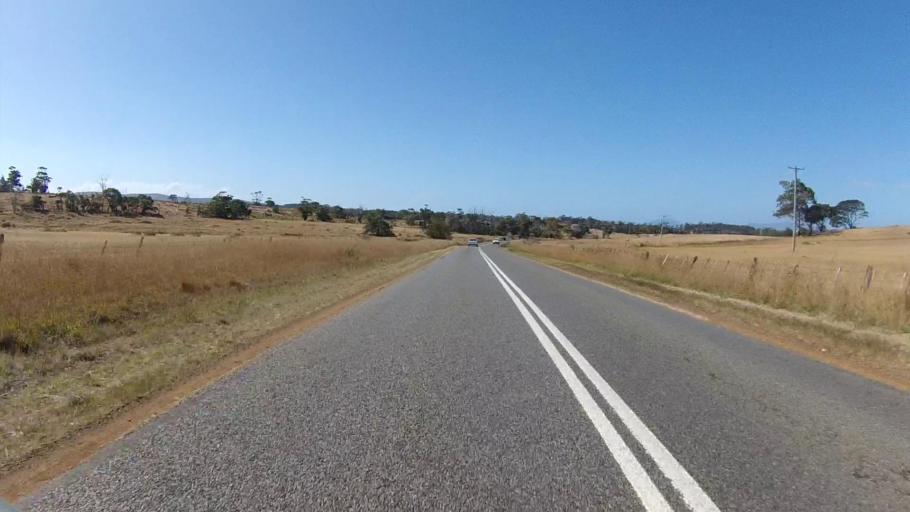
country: AU
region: Tasmania
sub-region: Sorell
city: Sorell
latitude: -42.2997
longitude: 147.9812
